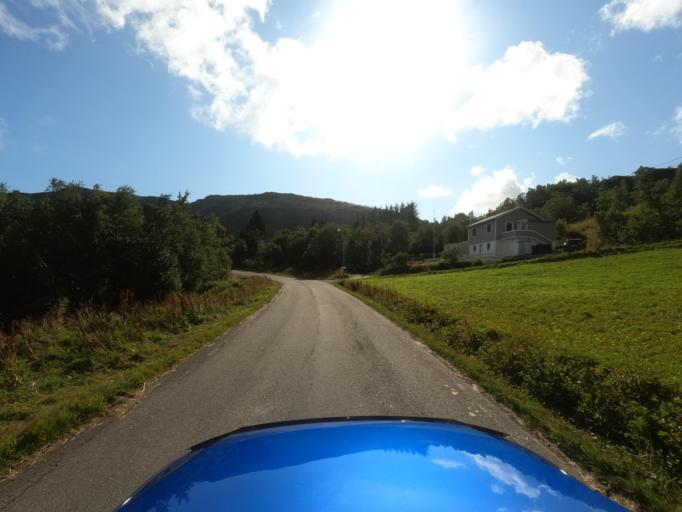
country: NO
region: Nordland
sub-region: Vestvagoy
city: Evjen
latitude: 68.1596
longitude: 13.7814
